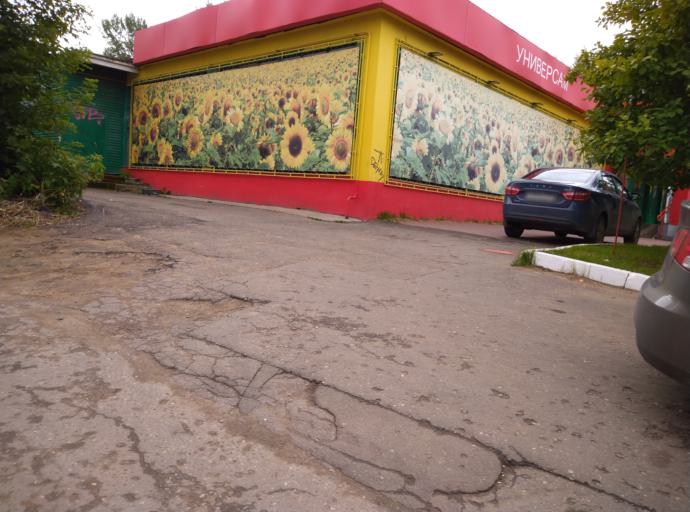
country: RU
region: Kostroma
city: Oktyabr'skiy
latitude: 57.7473
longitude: 40.9680
